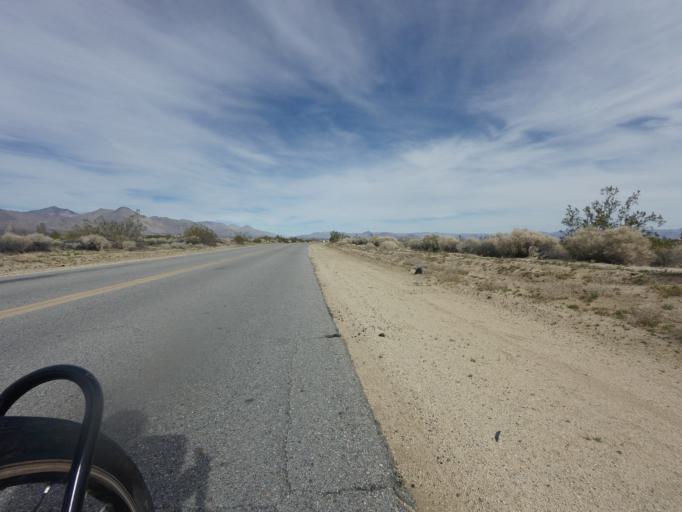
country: US
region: California
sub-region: Kern County
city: Inyokern
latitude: 35.7157
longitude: -117.8331
